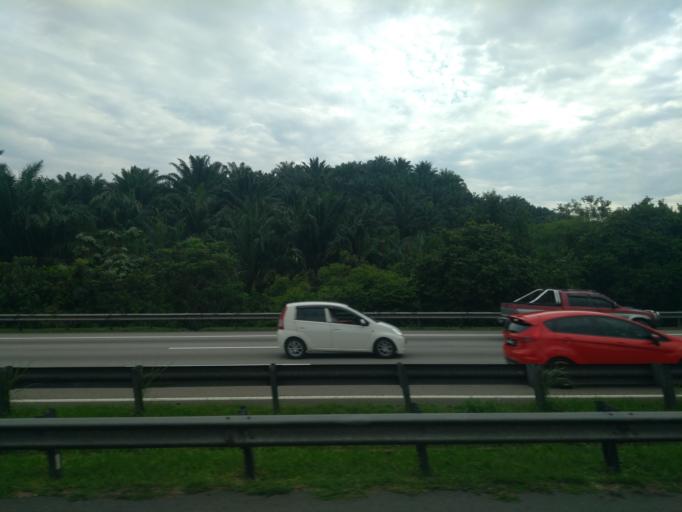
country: MY
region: Negeri Sembilan
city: Tampin
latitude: 2.4590
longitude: 102.1625
